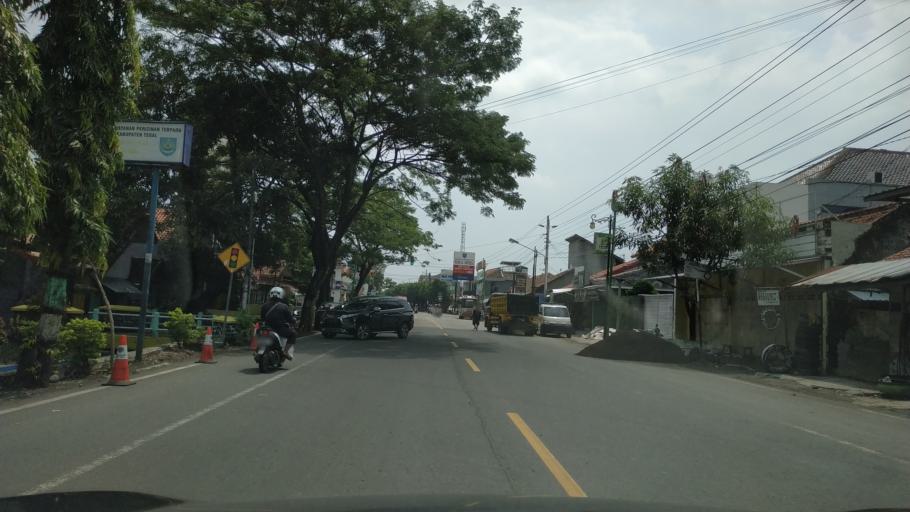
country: ID
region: Central Java
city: Slawi
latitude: -6.9931
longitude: 109.1415
